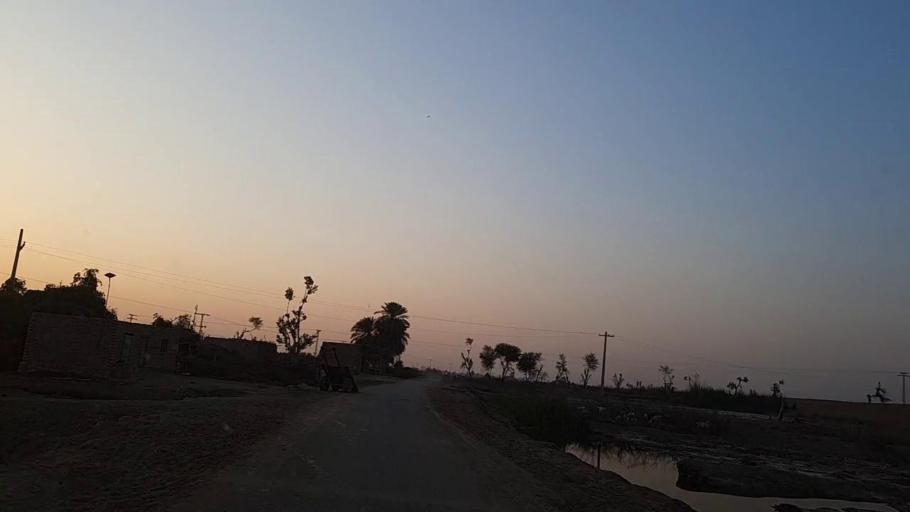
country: PK
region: Sindh
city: Bhit Shah
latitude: 25.9263
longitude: 68.4844
